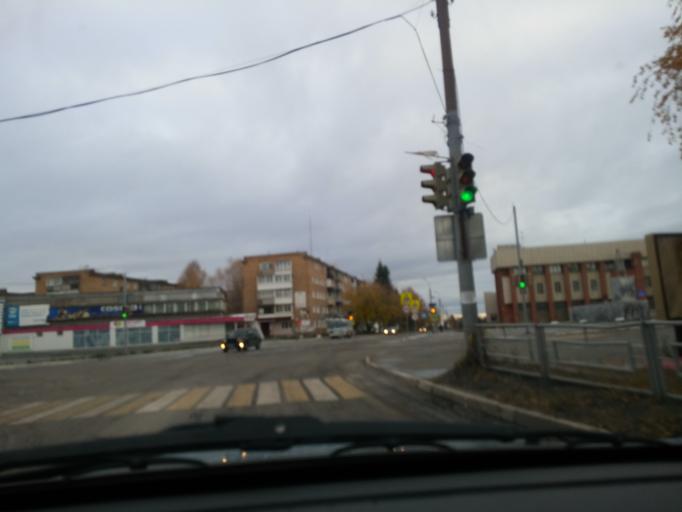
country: RU
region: Sverdlovsk
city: Turinsk
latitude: 58.0523
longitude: 63.6921
